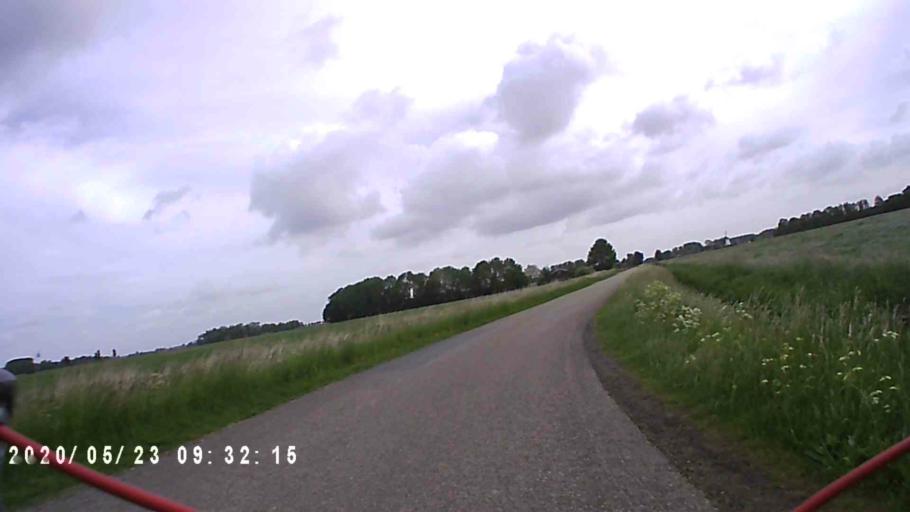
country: NL
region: Groningen
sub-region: Gemeente Bedum
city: Bedum
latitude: 53.2950
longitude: 6.7173
